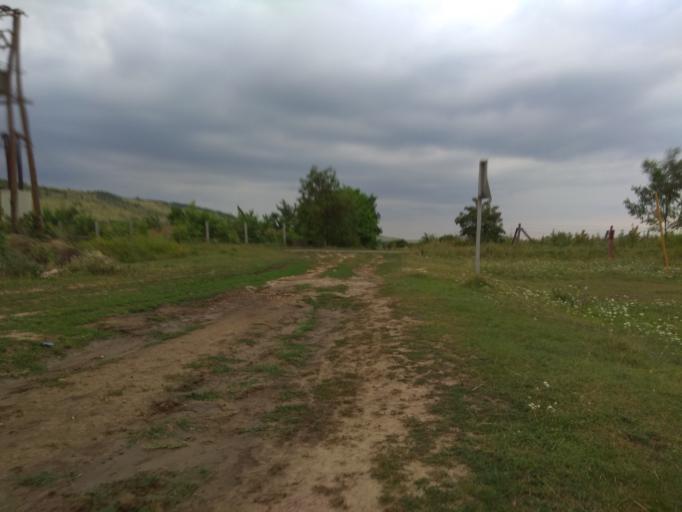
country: HU
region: Borsod-Abauj-Zemplen
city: Bekecs
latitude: 48.1560
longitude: 21.1261
